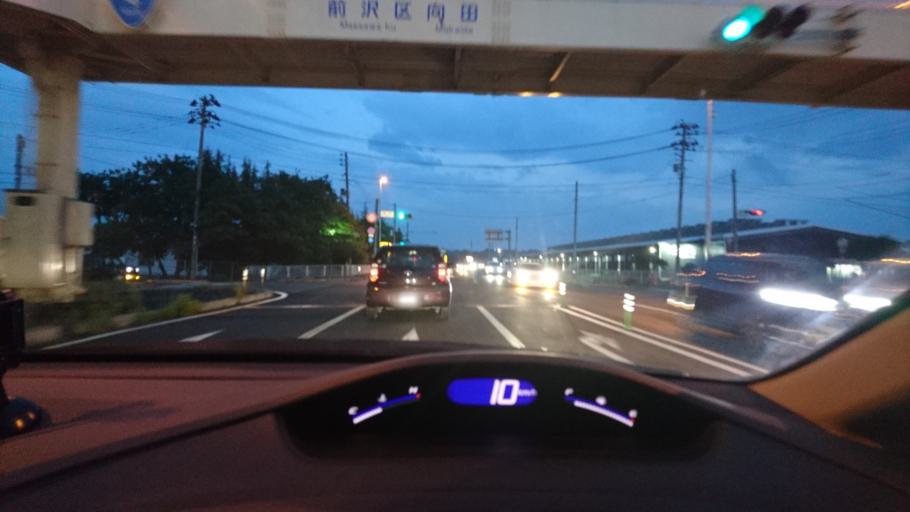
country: JP
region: Iwate
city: Mizusawa
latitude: 39.0465
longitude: 141.1303
